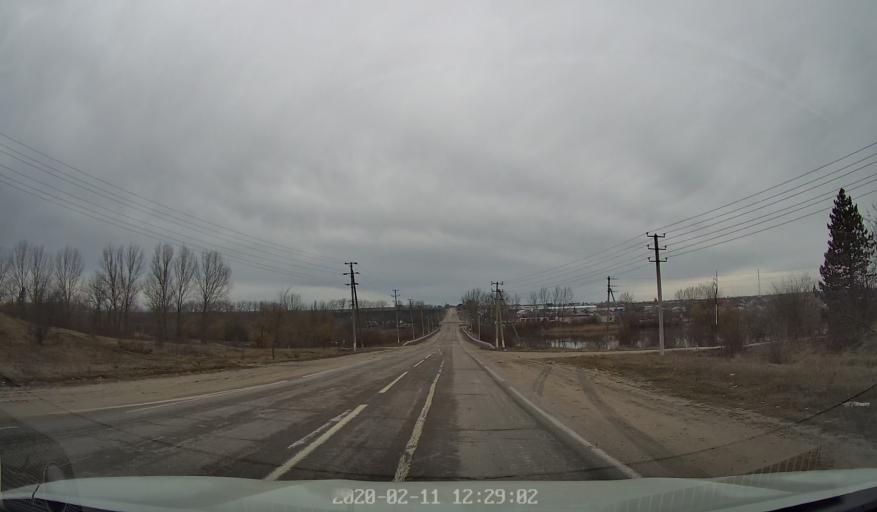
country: MD
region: Raionul Edinet
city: Edinet
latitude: 48.1509
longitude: 27.2932
